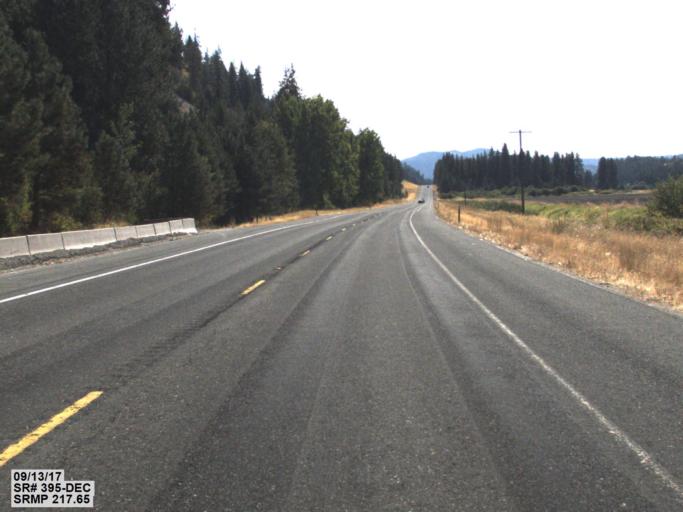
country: US
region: Washington
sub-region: Stevens County
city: Chewelah
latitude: 48.3829
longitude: -117.8420
